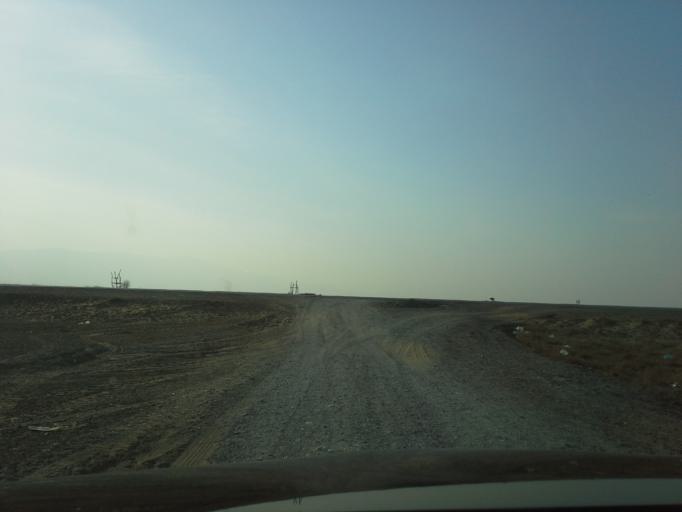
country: TM
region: Ahal
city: Abadan
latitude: 38.1725
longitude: 58.0370
